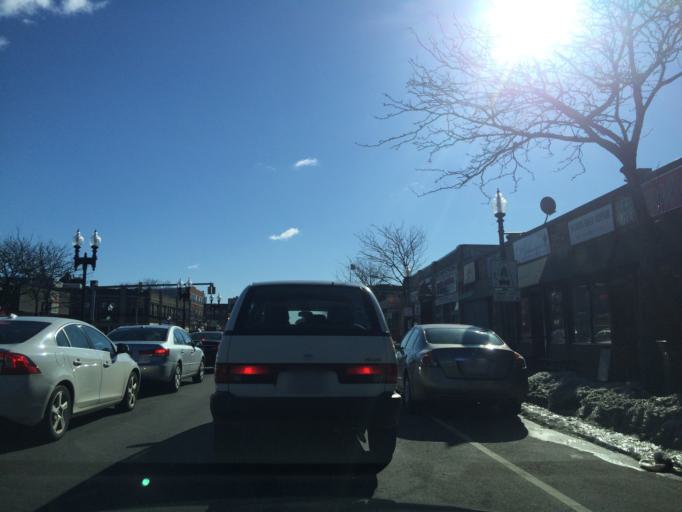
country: US
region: Massachusetts
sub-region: Norfolk County
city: Brookline
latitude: 42.3531
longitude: -71.1331
